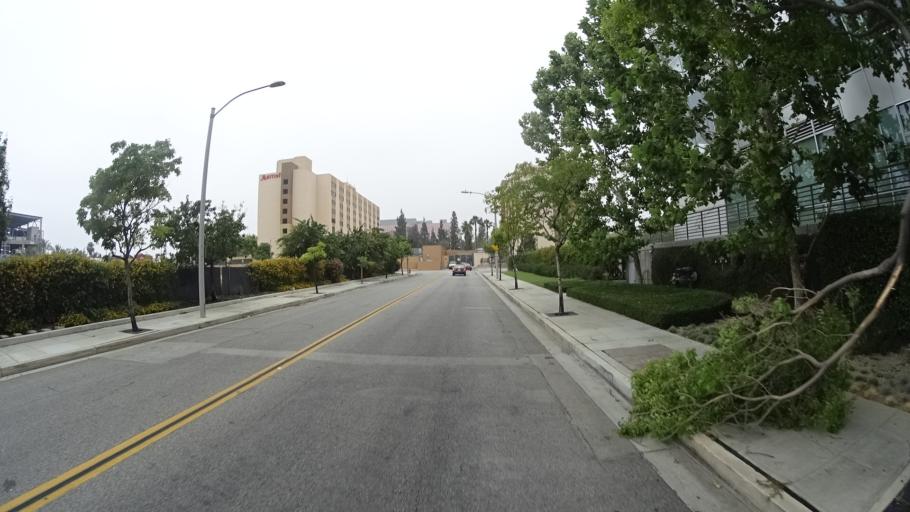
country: US
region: California
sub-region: Los Angeles County
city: North Hollywood
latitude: 34.1927
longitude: -118.3478
